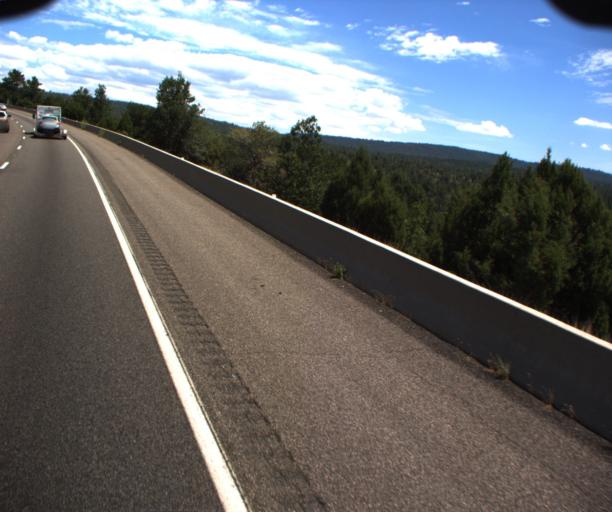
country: US
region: Arizona
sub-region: Yavapai County
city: Village of Oak Creek (Big Park)
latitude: 34.7946
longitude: -111.5899
